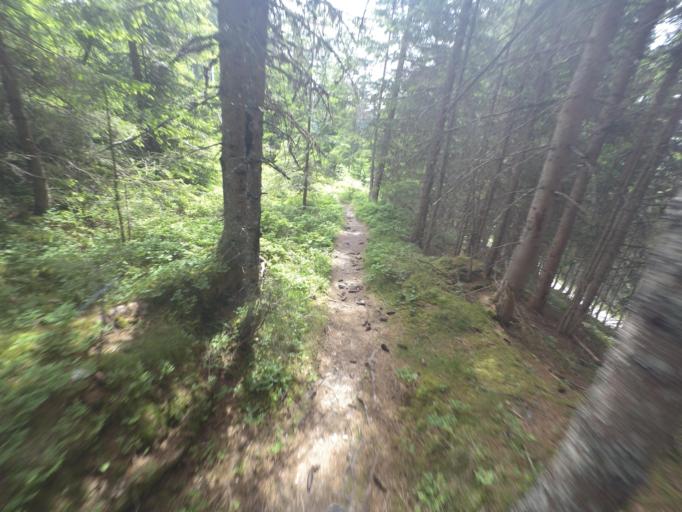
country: AT
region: Salzburg
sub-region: Politischer Bezirk Sankt Johann im Pongau
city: Muhlbach am Hochkonig
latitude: 47.3636
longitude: 13.1033
